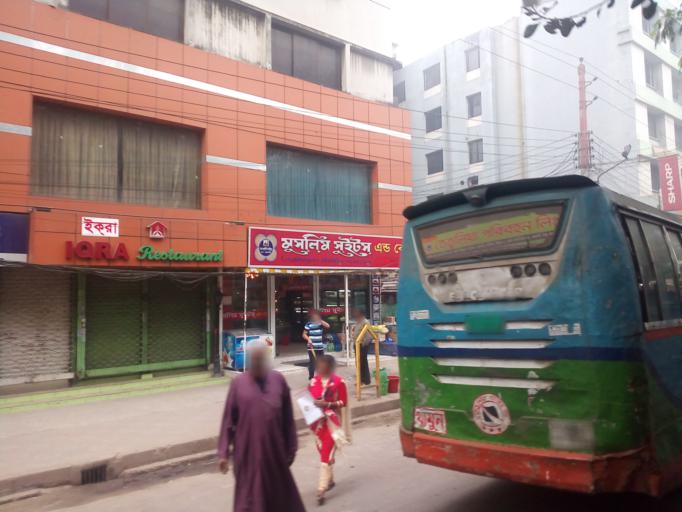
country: BD
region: Dhaka
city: Azimpur
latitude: 23.7900
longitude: 90.3757
